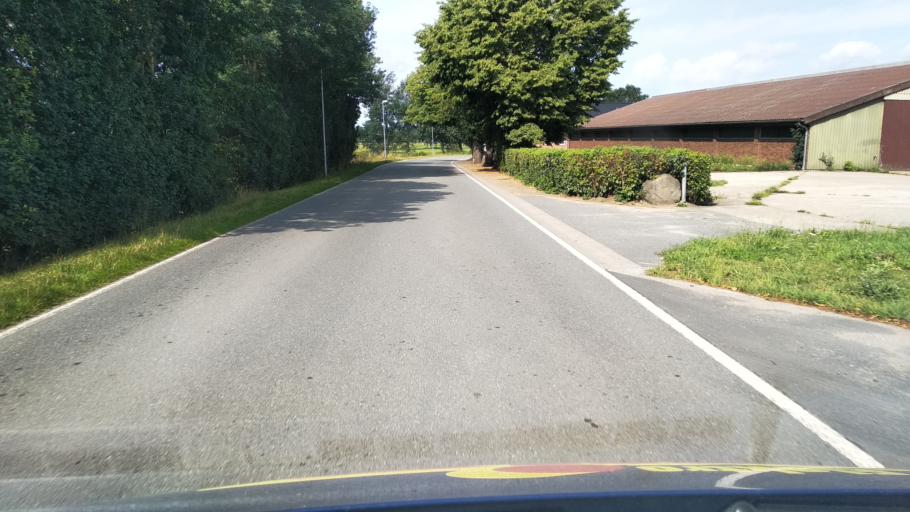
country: DE
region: Schleswig-Holstein
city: Brekendorf
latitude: 54.4225
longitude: 9.6241
